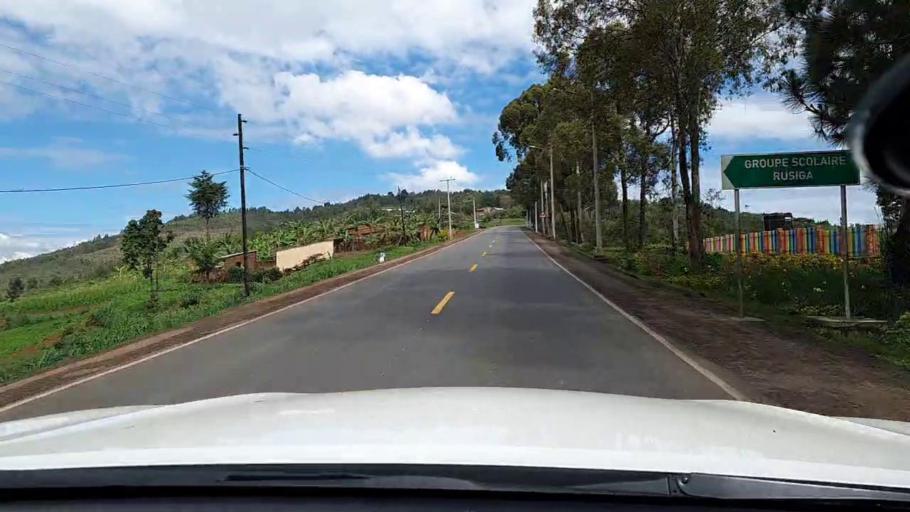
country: RW
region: Kigali
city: Kigali
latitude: -1.8321
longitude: 29.9505
